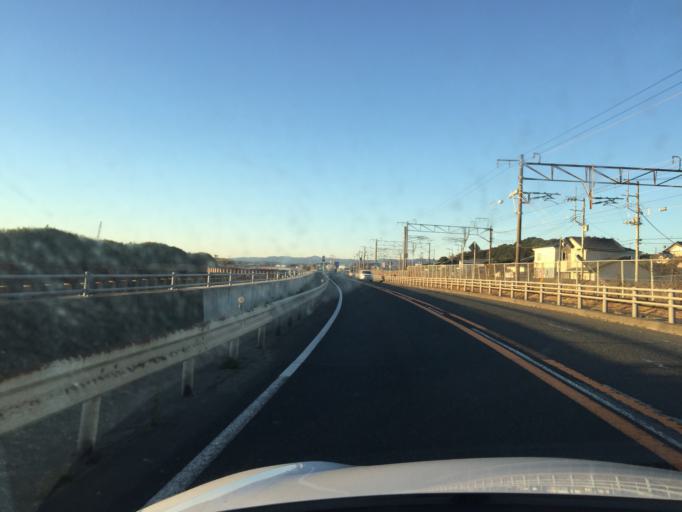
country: JP
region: Ibaraki
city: Kitaibaraki
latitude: 36.7946
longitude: 140.7530
